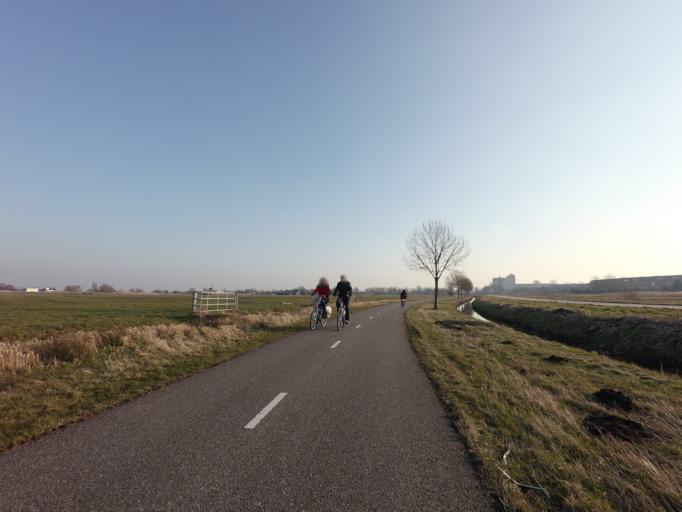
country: NL
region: North Holland
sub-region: Gemeente Haarlem
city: Haarlem
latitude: 52.3598
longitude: 4.6694
